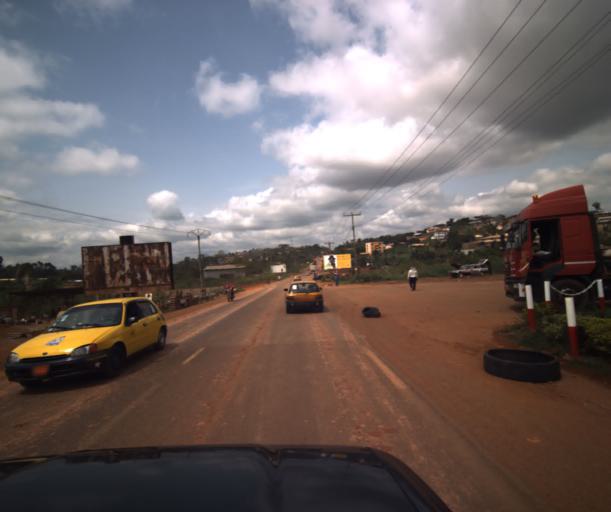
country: CM
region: Centre
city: Yaounde
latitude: 3.7997
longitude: 11.5042
